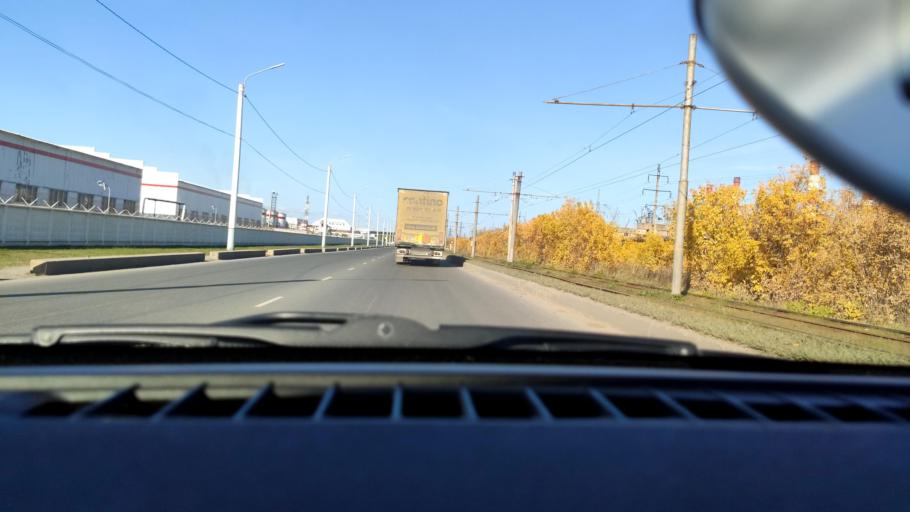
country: RU
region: Perm
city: Gamovo
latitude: 57.9175
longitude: 56.1496
